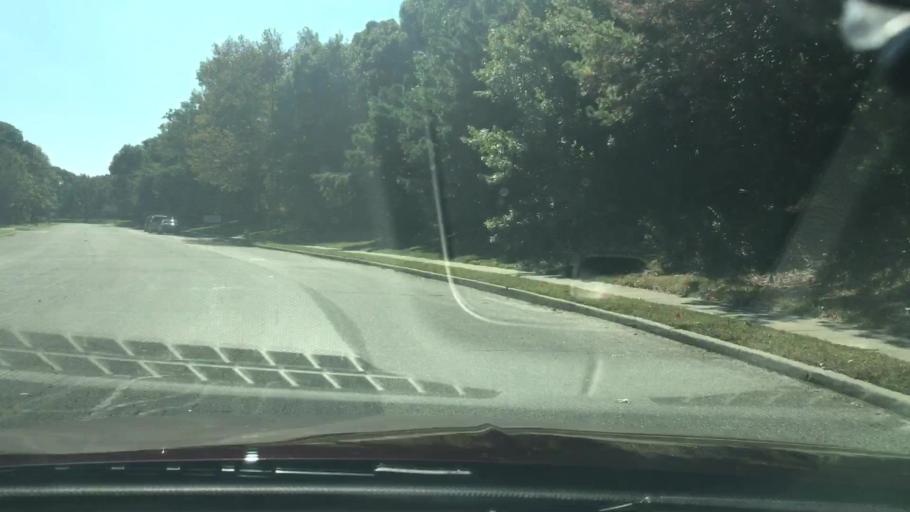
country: US
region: New York
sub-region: Suffolk County
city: Holtsville
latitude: 40.8040
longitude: -73.0397
